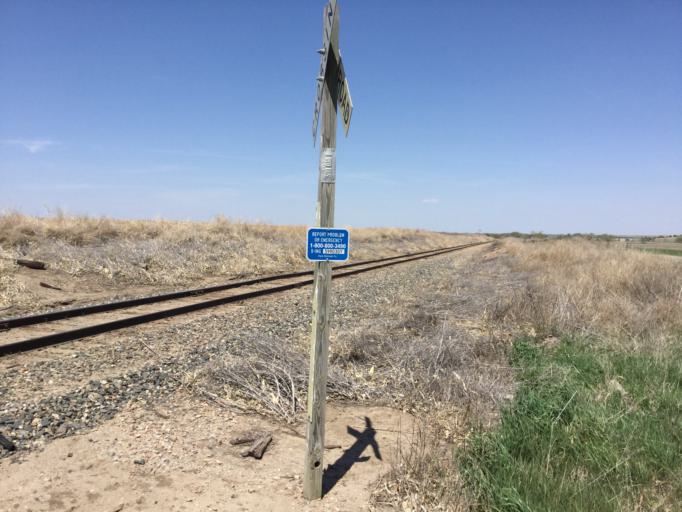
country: US
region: Kansas
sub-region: Decatur County
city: Oberlin
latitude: 39.6544
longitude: -100.3490
